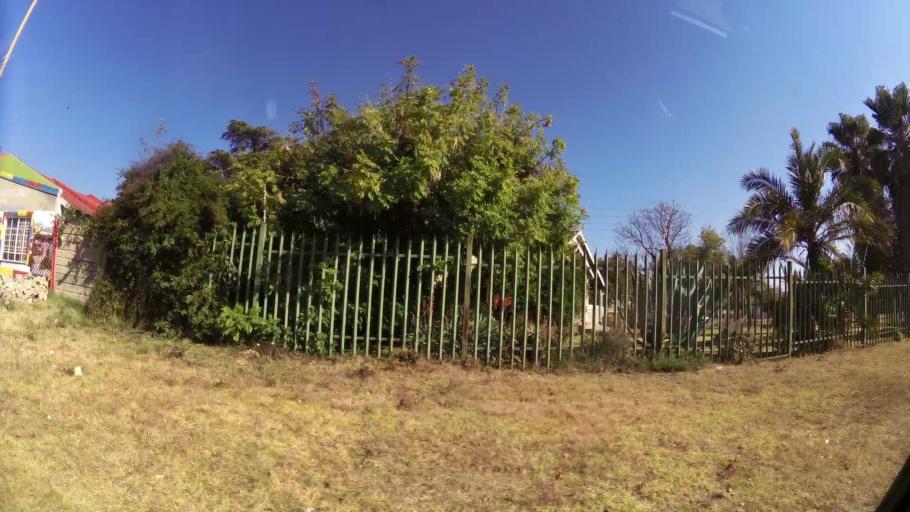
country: ZA
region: Gauteng
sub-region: Ekurhuleni Metropolitan Municipality
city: Germiston
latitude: -26.2430
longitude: 28.1097
